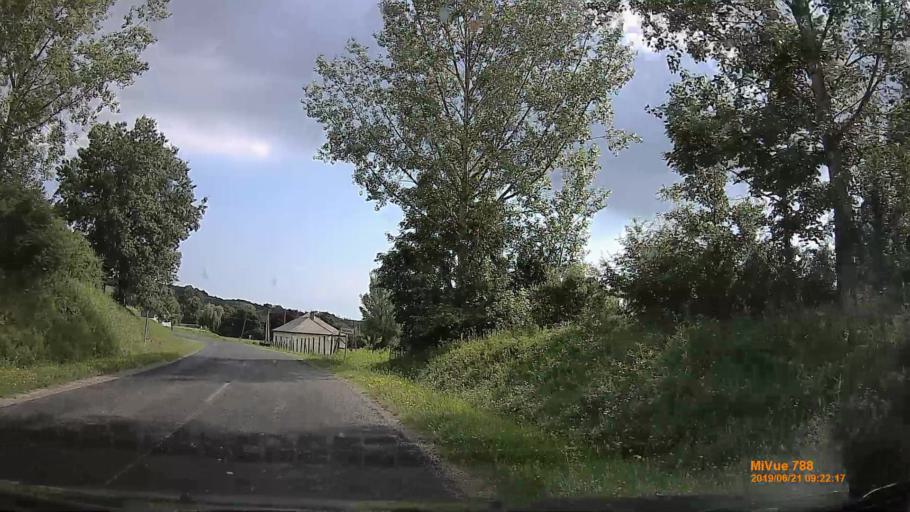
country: HU
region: Somogy
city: Taszar
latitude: 46.2454
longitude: 17.8904
